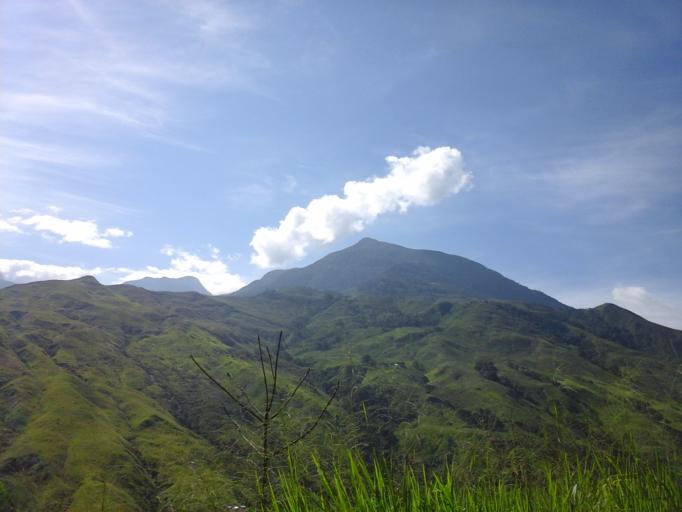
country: CO
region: Cesar
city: Agustin Codazzi
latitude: 9.9423
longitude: -73.0934
